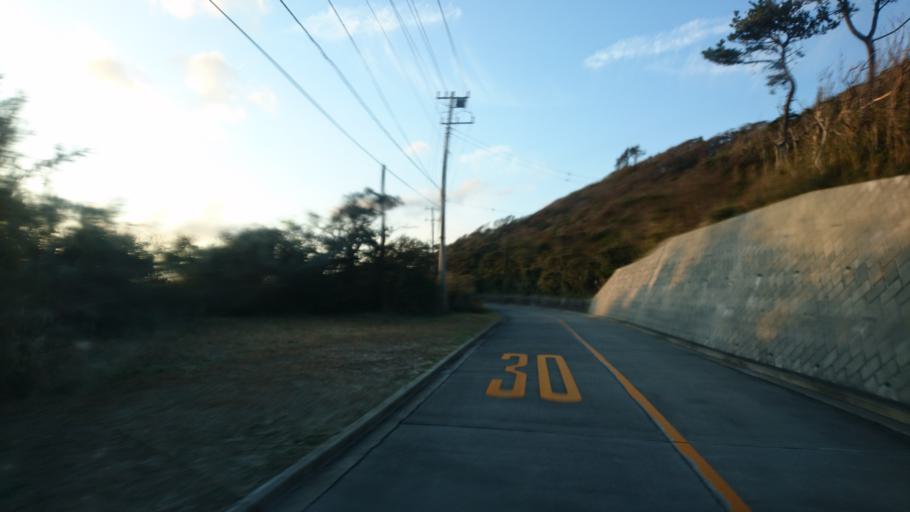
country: JP
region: Shizuoka
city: Shimoda
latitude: 34.3630
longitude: 139.2459
